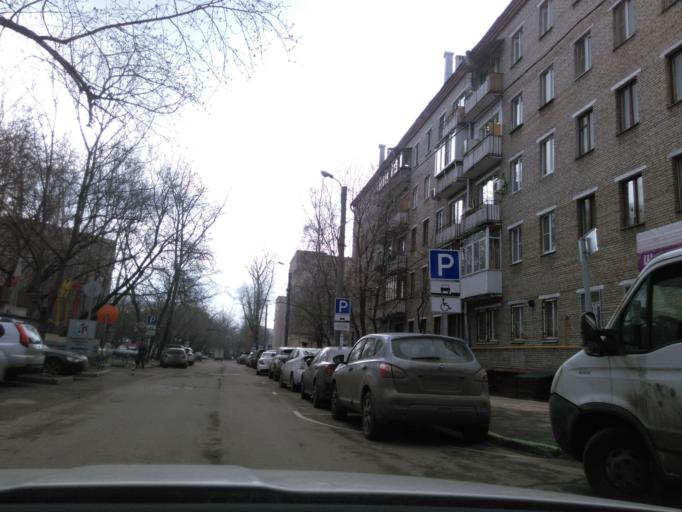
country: RU
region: Moskovskaya
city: Dorogomilovo
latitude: 55.7778
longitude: 37.5725
